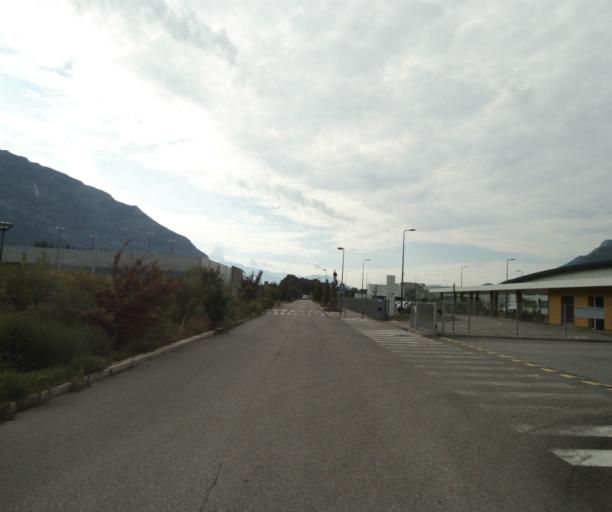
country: FR
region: Rhone-Alpes
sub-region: Departement de l'Isere
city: Fontanil-Cornillon
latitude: 45.2430
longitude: 5.6636
